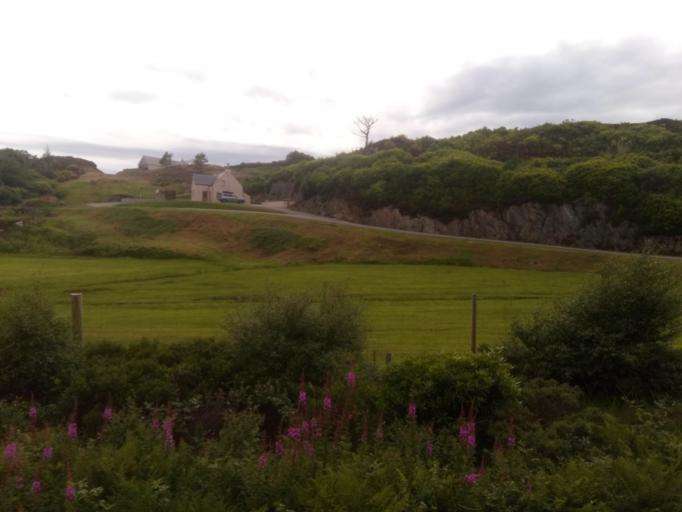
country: GB
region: Scotland
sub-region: Argyll and Bute
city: Isle Of Mull
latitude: 56.9654
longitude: -5.8159
